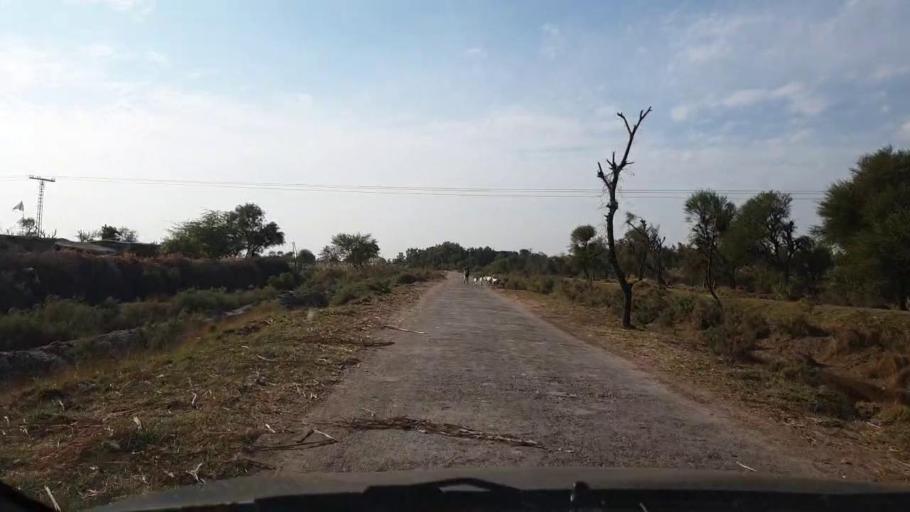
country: PK
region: Sindh
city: Jhol
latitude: 25.9732
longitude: 68.8312
